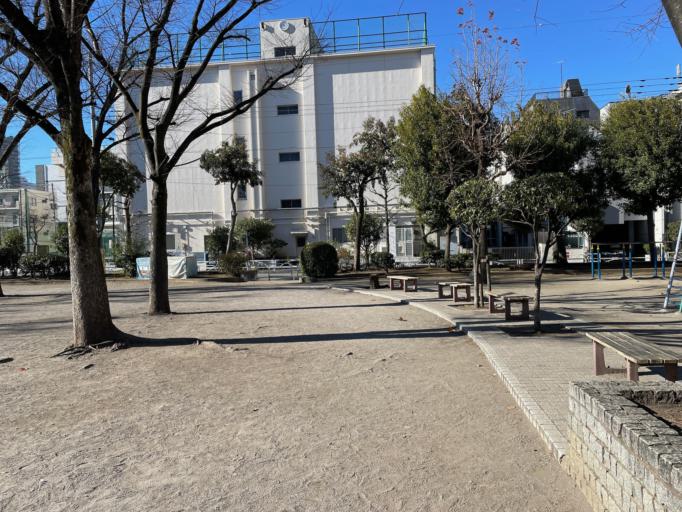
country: JP
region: Tokyo
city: Urayasu
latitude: 35.7027
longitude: 139.8014
